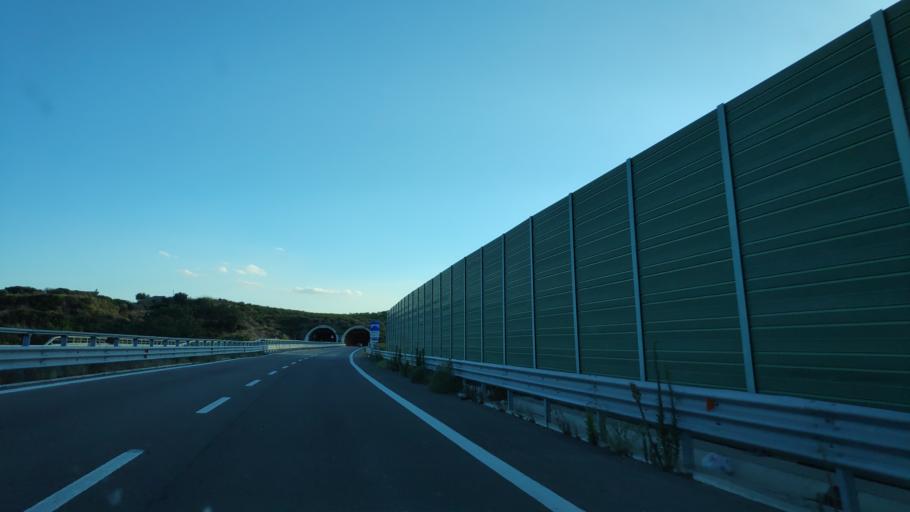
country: IT
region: Calabria
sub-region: Provincia di Reggio Calabria
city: Siderno
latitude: 38.2779
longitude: 16.2750
